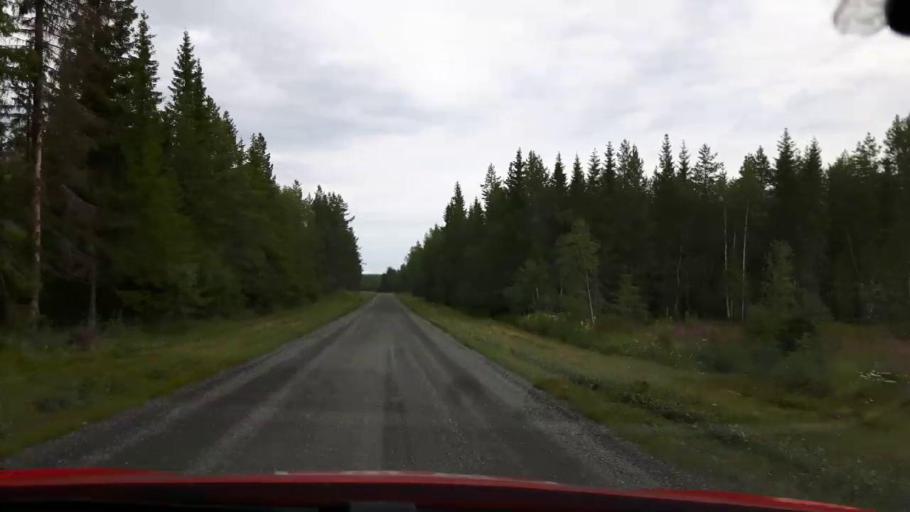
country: SE
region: Jaemtland
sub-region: Stroemsunds Kommun
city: Stroemsund
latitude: 63.7453
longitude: 15.5838
